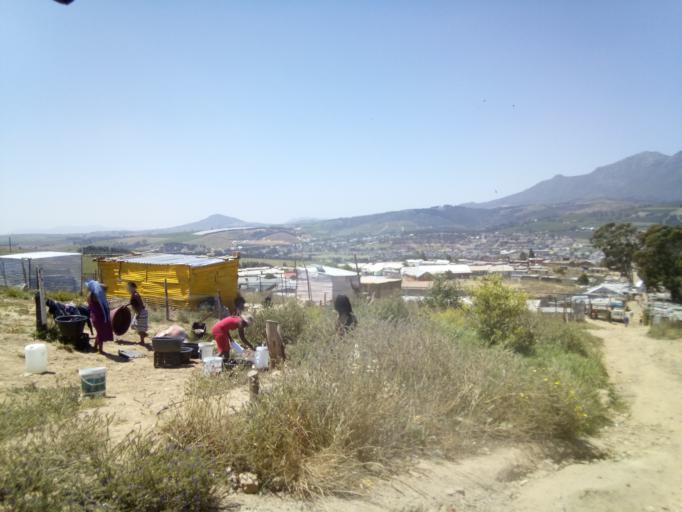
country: ZA
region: Western Cape
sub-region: Cape Winelands District Municipality
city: Stellenbosch
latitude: -33.9240
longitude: 18.8408
